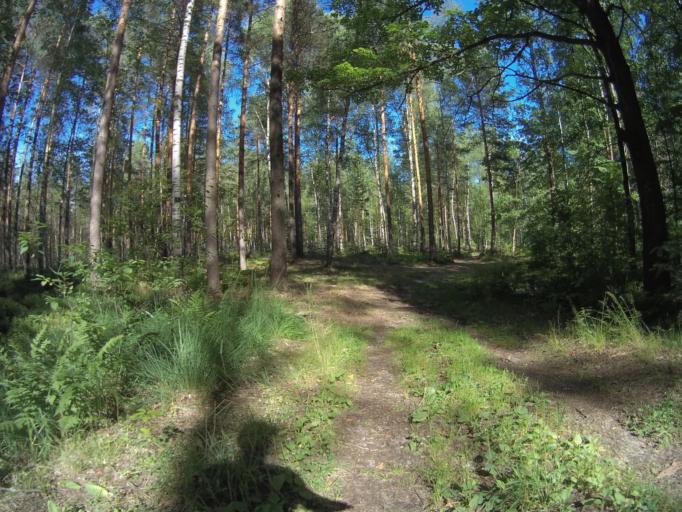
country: RU
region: Vladimir
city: Raduzhnyy
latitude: 56.0536
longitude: 40.3525
